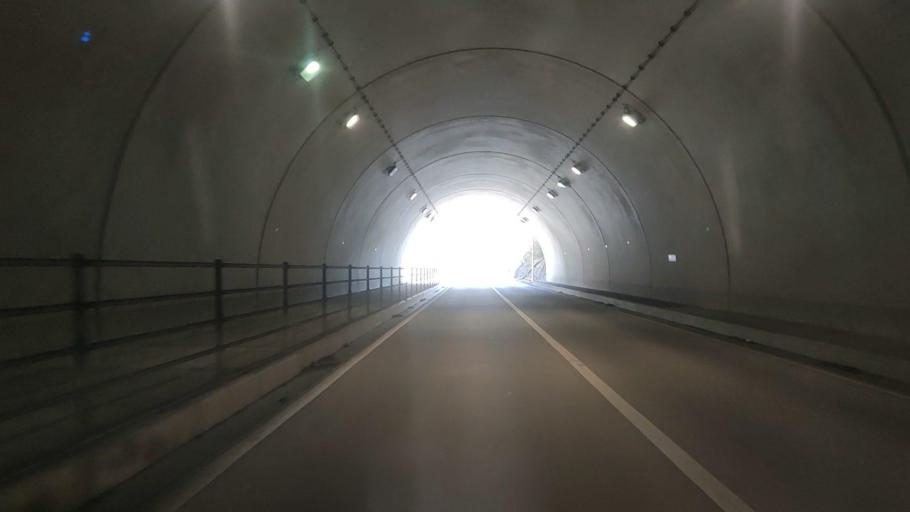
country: JP
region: Oita
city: Saiki
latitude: 32.8045
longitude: 131.8979
